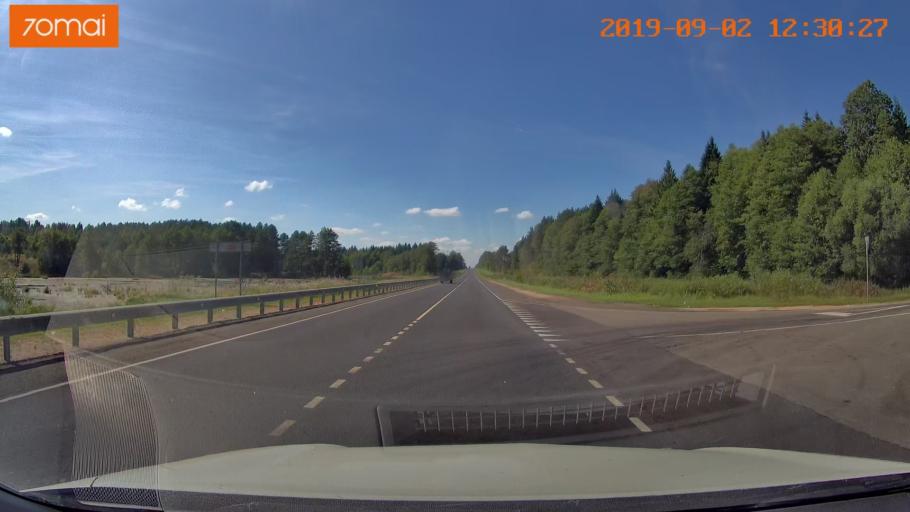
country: RU
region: Smolensk
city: Shumyachi
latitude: 53.8319
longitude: 32.4740
